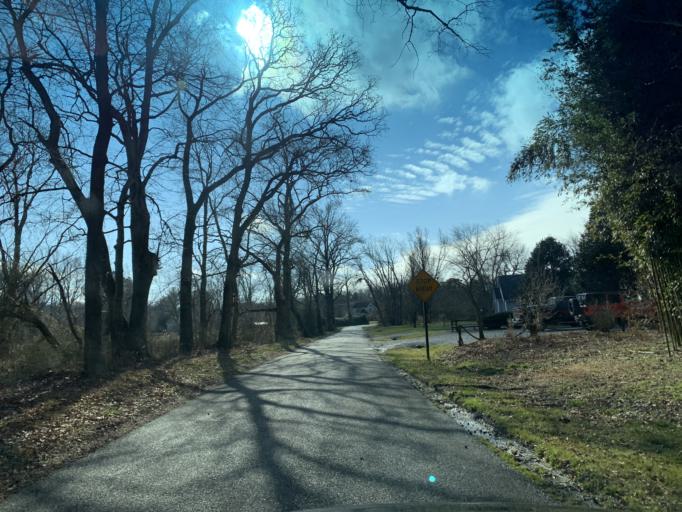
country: US
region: Delaware
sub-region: Sussex County
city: Selbyville
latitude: 38.4422
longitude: -75.1902
